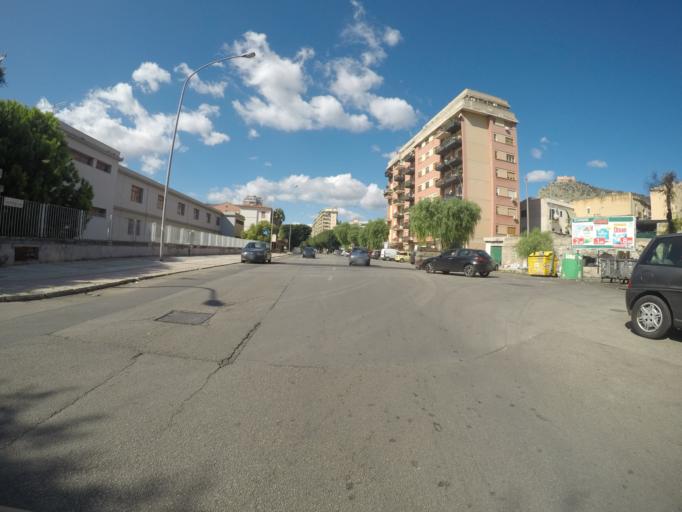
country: IT
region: Sicily
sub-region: Palermo
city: Palermo
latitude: 38.1443
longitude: 13.3662
